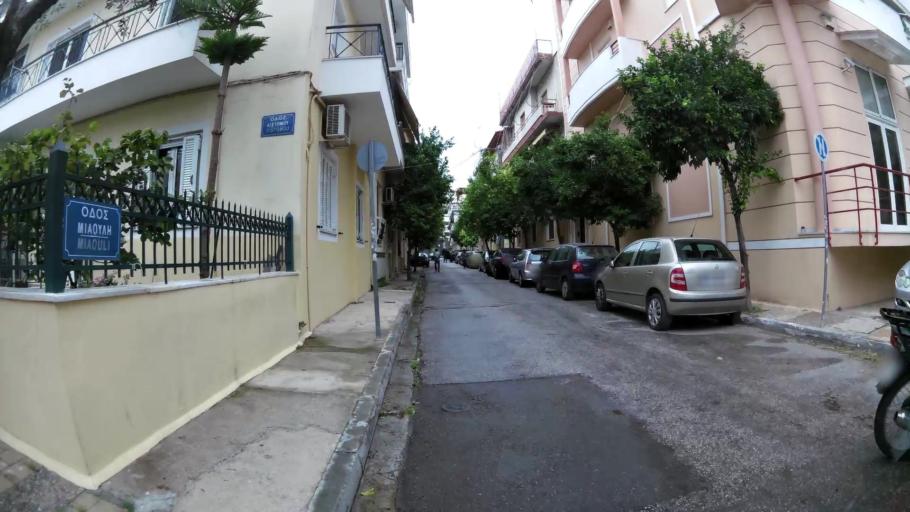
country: GR
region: Attica
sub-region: Nomarchia Athinas
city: Agioi Anargyroi
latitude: 38.0284
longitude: 23.7149
